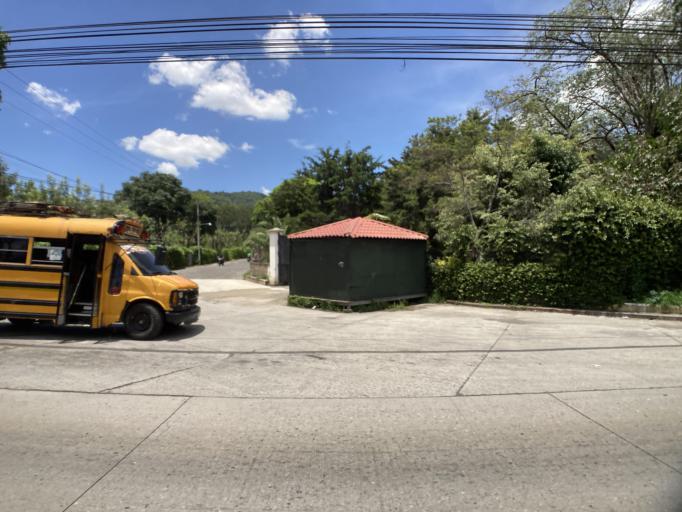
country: GT
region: Sacatepequez
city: Antigua Guatemala
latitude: 14.5426
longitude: -90.7294
